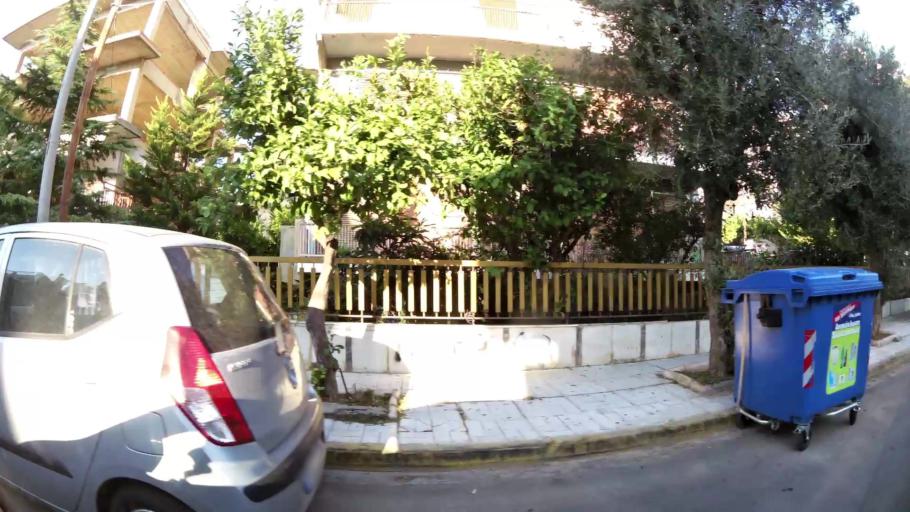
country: GR
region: Attica
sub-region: Nomarchia Athinas
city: Glyfada
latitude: 37.8854
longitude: 23.7729
